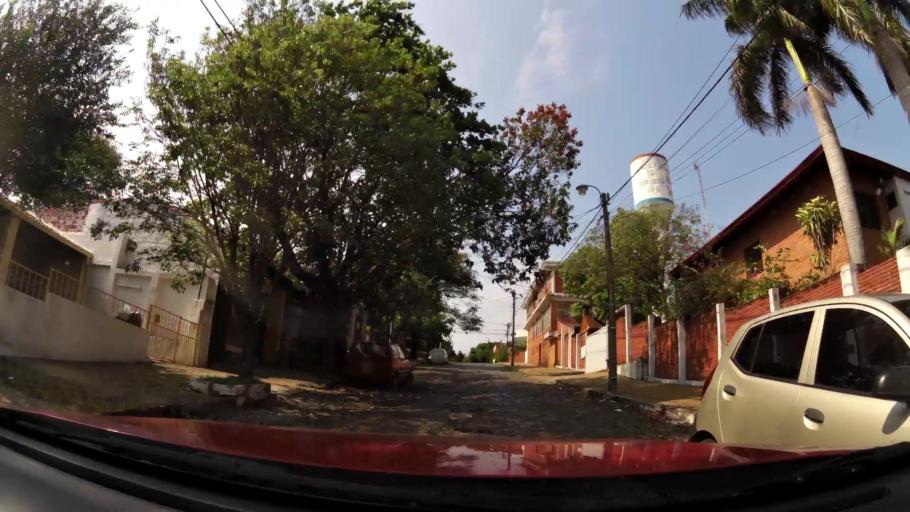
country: PY
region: Presidente Hayes
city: Nanawa
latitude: -25.2828
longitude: -57.6575
